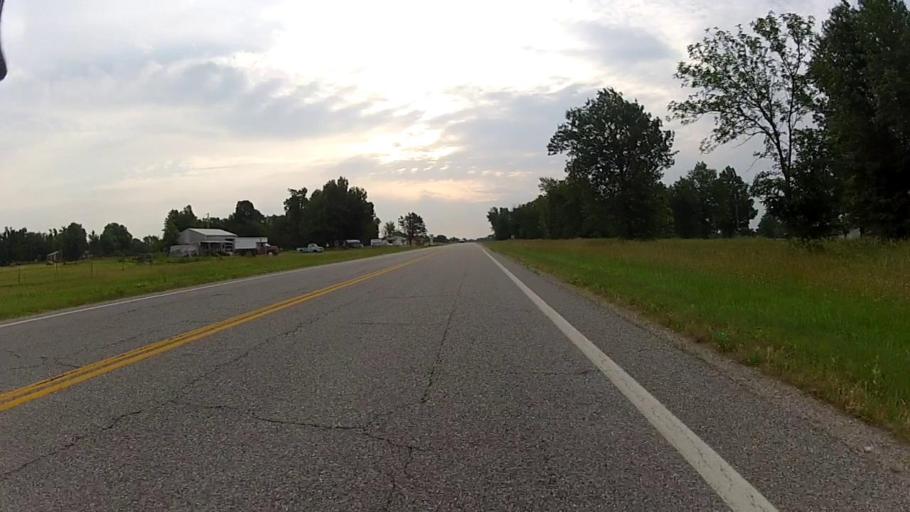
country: US
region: Kansas
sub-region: Labette County
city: Oswego
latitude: 37.1770
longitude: -94.9981
